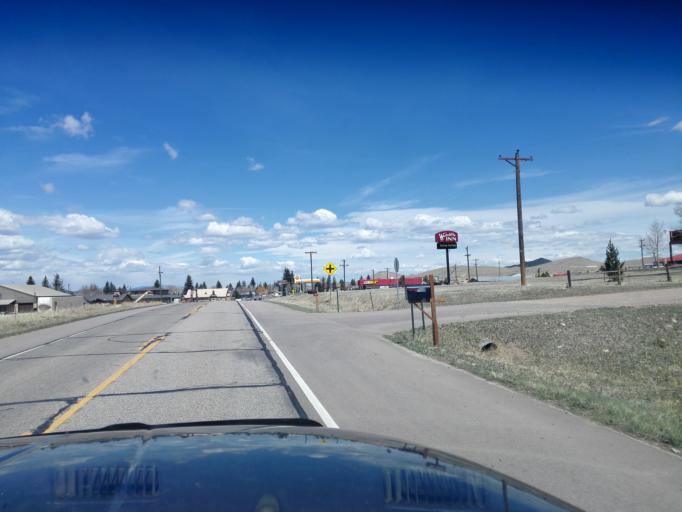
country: US
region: Colorado
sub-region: Custer County
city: Westcliffe
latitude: 38.1294
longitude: -105.4636
